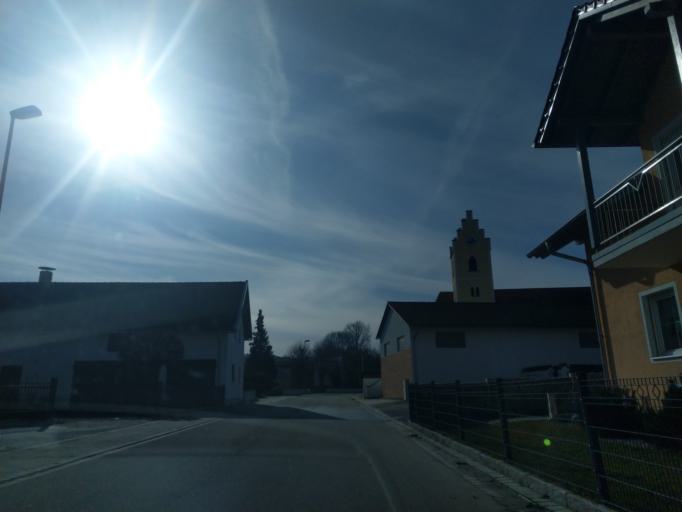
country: DE
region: Bavaria
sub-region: Lower Bavaria
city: Wallerfing
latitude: 48.6824
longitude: 12.8953
